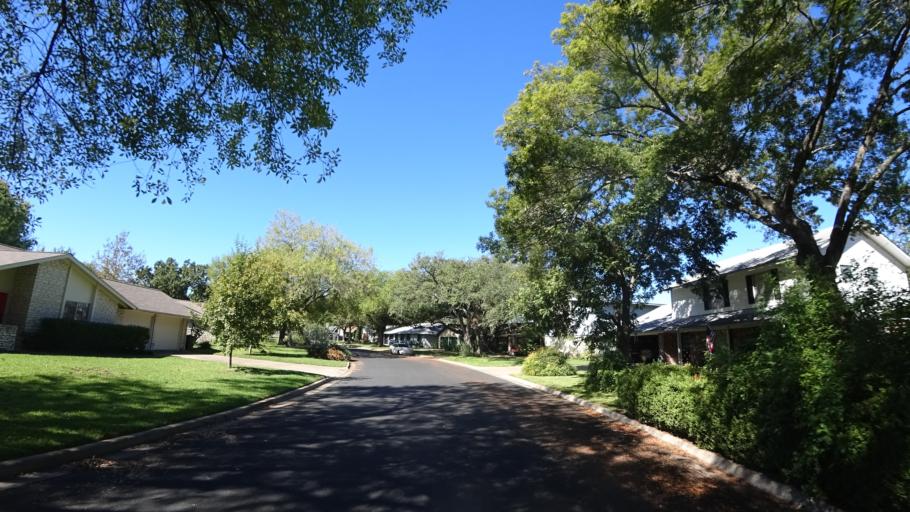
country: US
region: Texas
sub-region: Travis County
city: Austin
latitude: 30.3045
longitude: -97.6917
